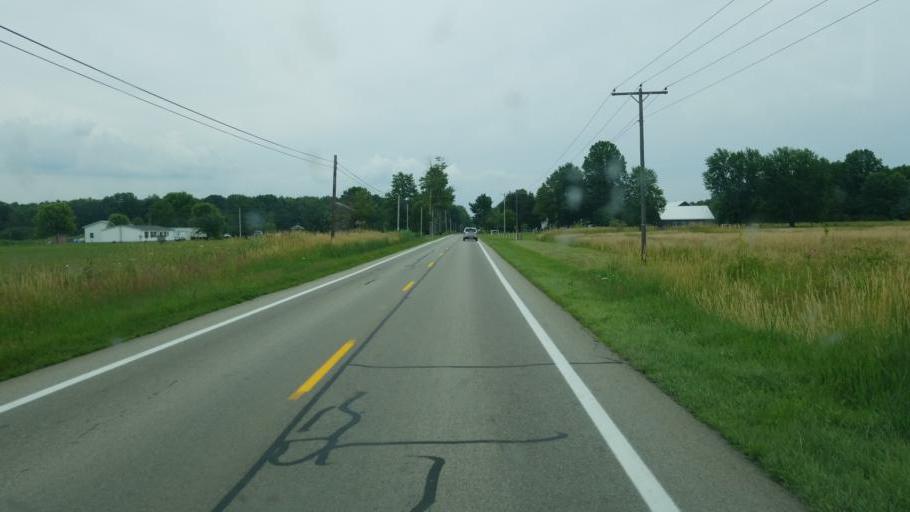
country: US
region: Ohio
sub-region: Ashtabula County
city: Orwell
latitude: 41.4616
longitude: -80.8021
